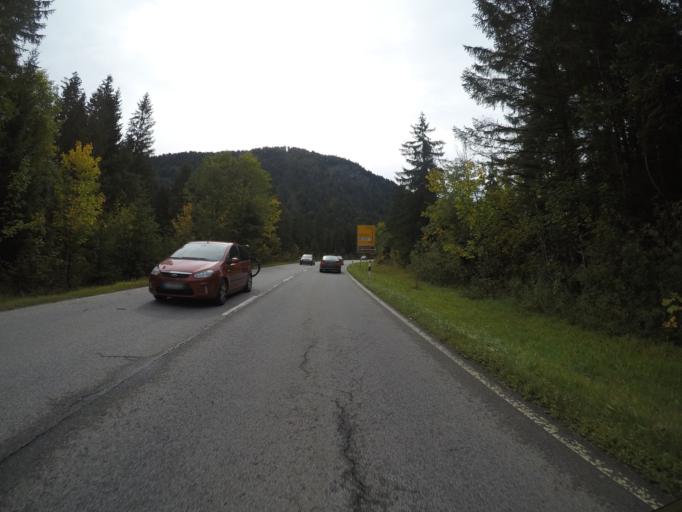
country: DE
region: Bavaria
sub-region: Upper Bavaria
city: Kreuth
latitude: 47.6285
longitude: 11.7465
